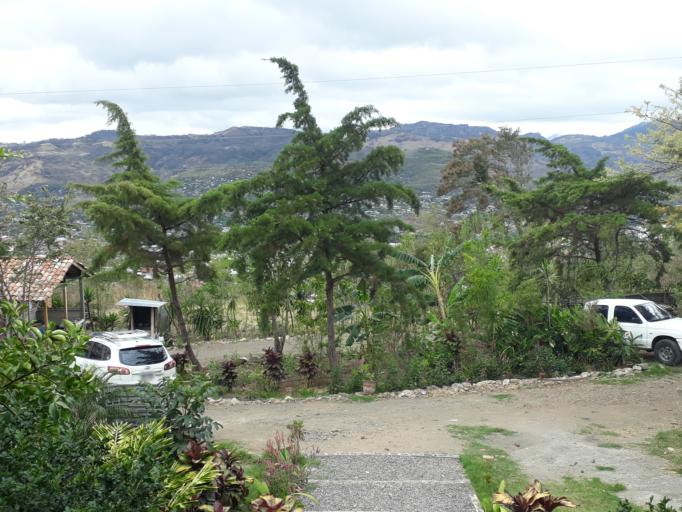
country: NI
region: Matagalpa
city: Matagalpa
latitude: 12.9175
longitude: -85.9116
